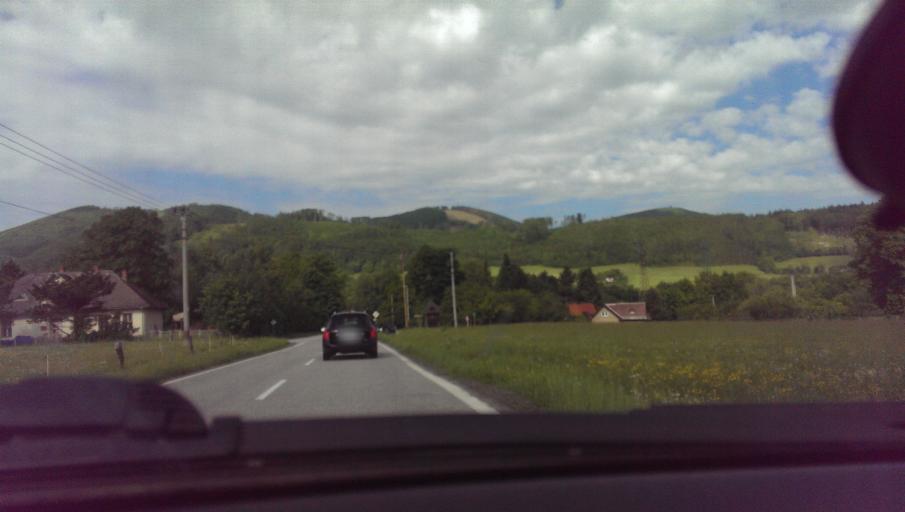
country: CZ
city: Trojanovice
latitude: 49.5159
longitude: 18.2062
